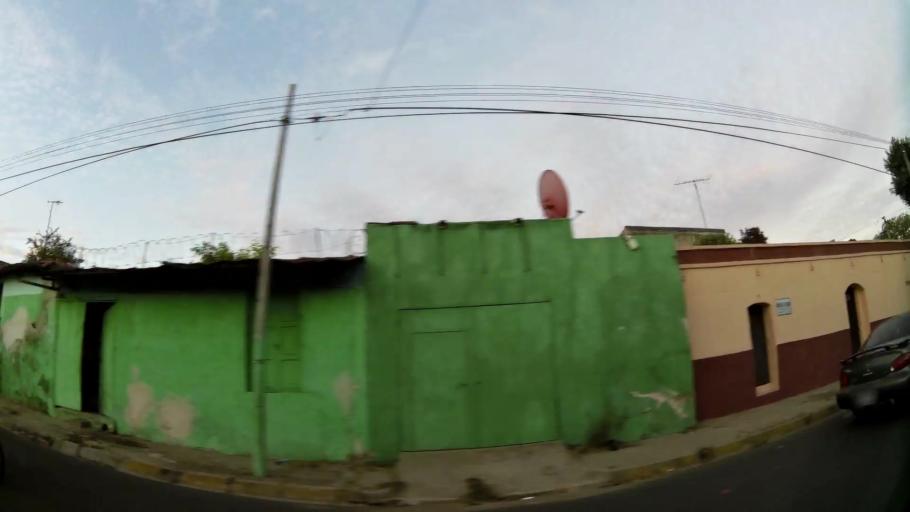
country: SV
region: Santa Ana
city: Santa Ana
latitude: 13.9871
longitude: -89.5497
